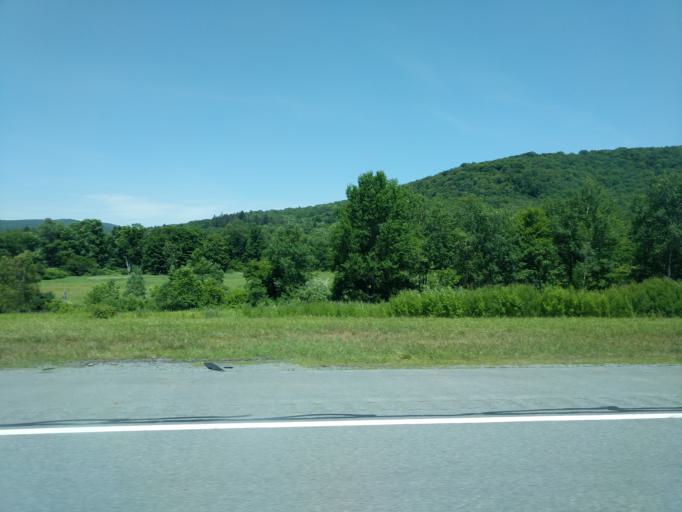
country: US
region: New York
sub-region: Sullivan County
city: Livingston Manor
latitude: 41.9146
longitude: -74.8376
